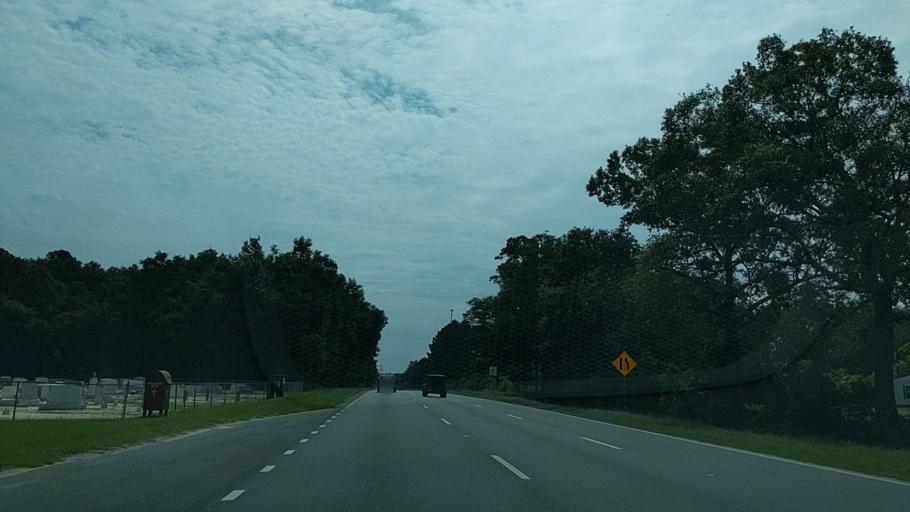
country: US
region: Georgia
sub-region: Effingham County
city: Rincon
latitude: 32.2501
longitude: -81.2120
